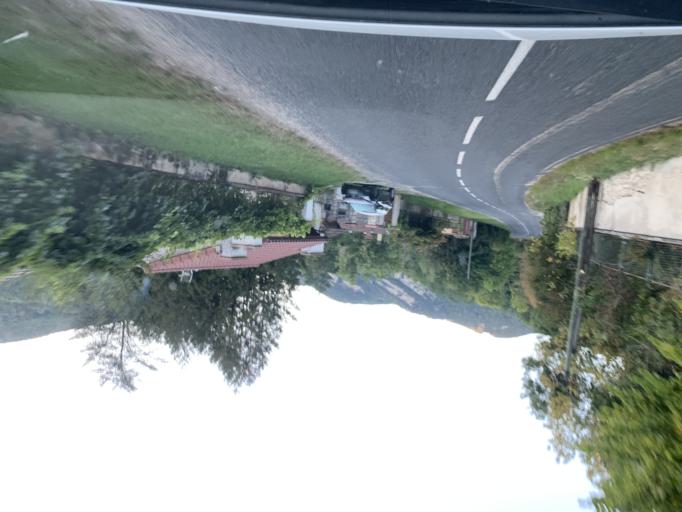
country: FR
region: Rhone-Alpes
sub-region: Departement de l'Ain
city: Saint-Rambert-en-Bugey
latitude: 45.9241
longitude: 5.4016
